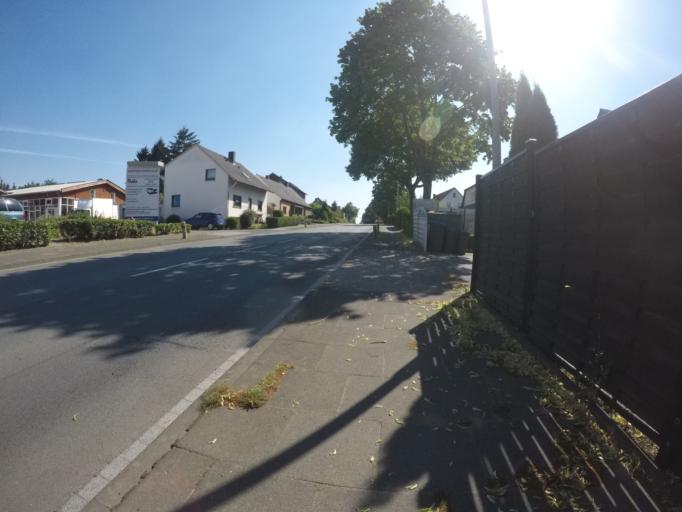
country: DE
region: North Rhine-Westphalia
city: Bad Oeynhausen
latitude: 52.1811
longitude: 8.7547
